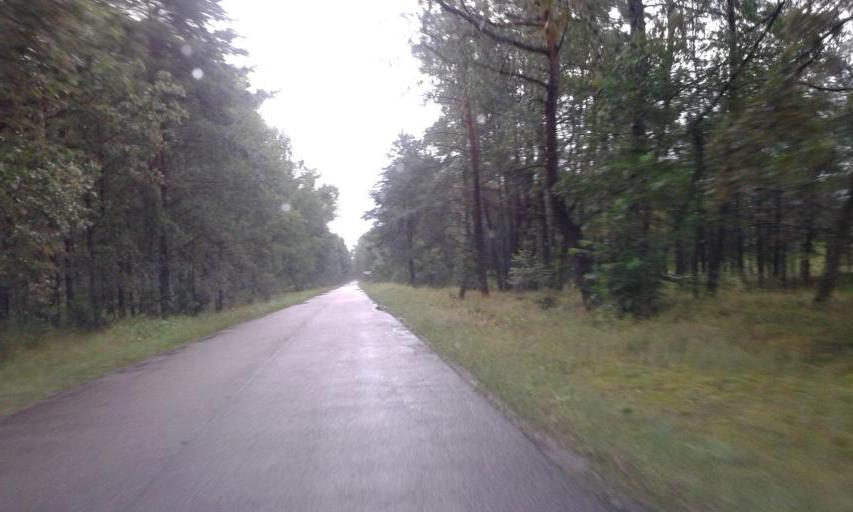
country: PL
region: West Pomeranian Voivodeship
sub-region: Powiat szczecinecki
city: Borne Sulinowo
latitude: 53.5381
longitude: 16.5036
